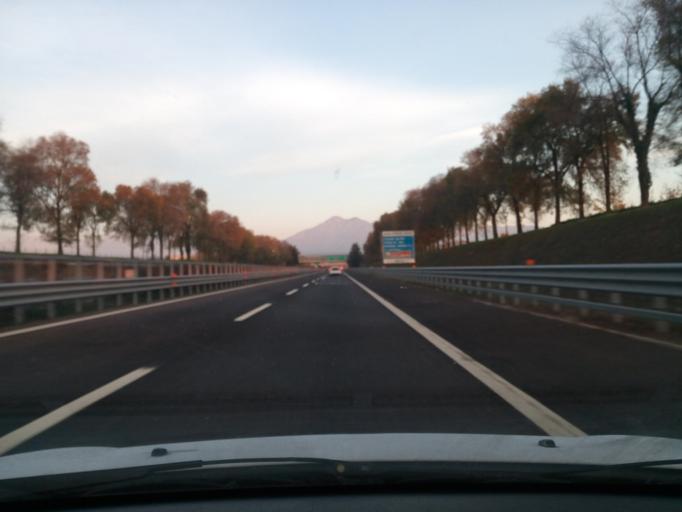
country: IT
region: Veneto
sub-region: Provincia di Vicenza
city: Thiene
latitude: 45.6772
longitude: 11.4659
